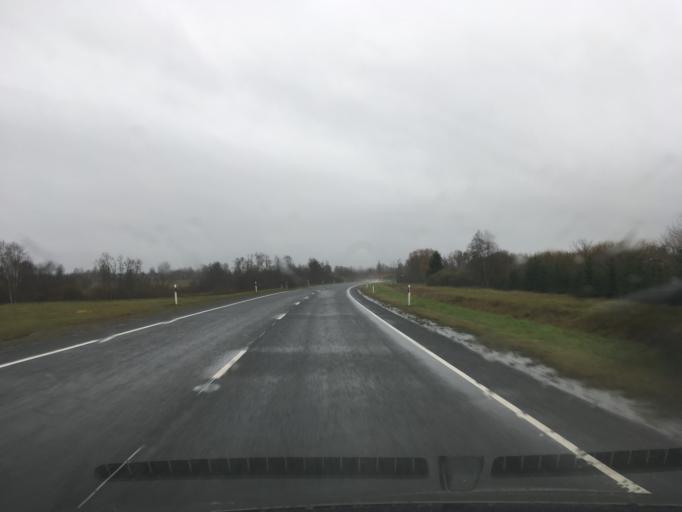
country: EE
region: Harju
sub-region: Nissi vald
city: Turba
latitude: 58.9223
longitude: 24.1125
